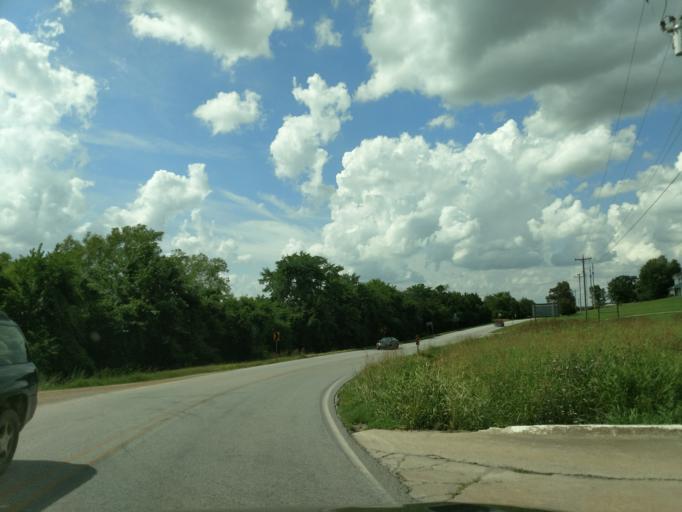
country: US
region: Arkansas
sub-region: Carroll County
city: Berryville
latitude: 36.3927
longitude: -93.5659
